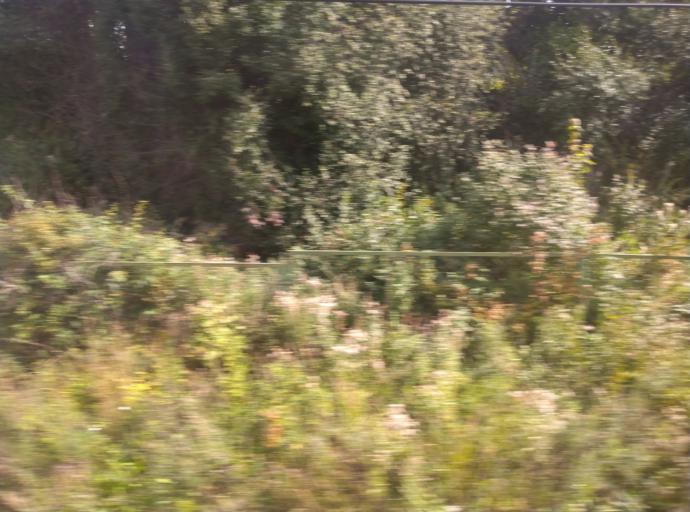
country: RU
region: Leningrad
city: Krasnyy Bor
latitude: 59.6848
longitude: 30.6956
